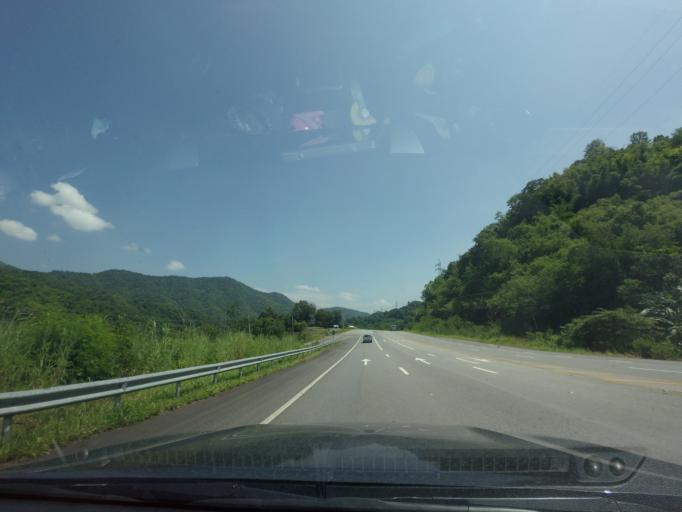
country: TH
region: Phetchabun
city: Lom Sak
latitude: 16.7799
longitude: 101.1063
